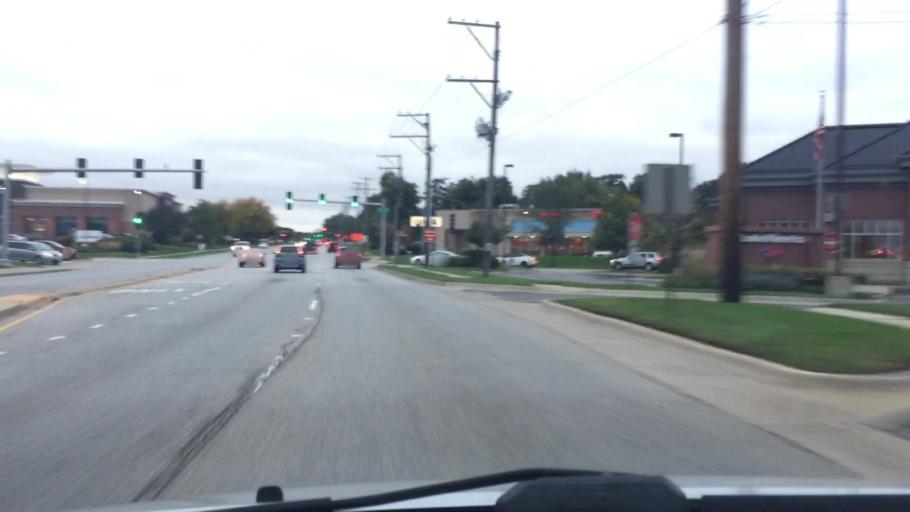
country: US
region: Illinois
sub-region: Kane County
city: West Dundee
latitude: 42.1004
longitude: -88.2872
